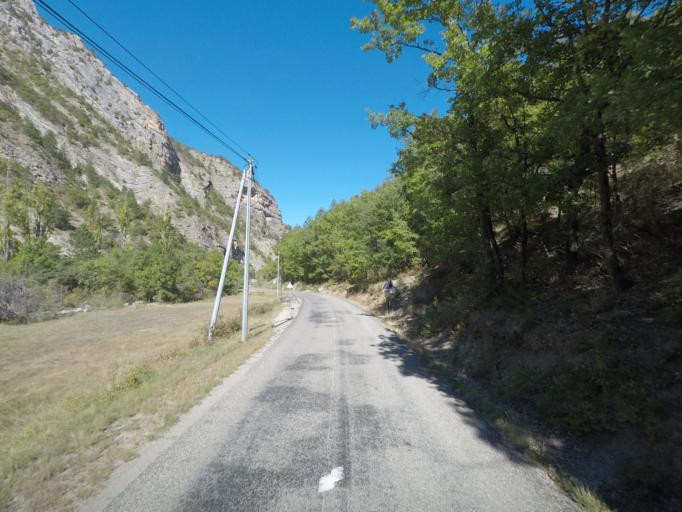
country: FR
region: Rhone-Alpes
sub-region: Departement de la Drome
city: Die
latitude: 44.6488
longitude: 5.2887
